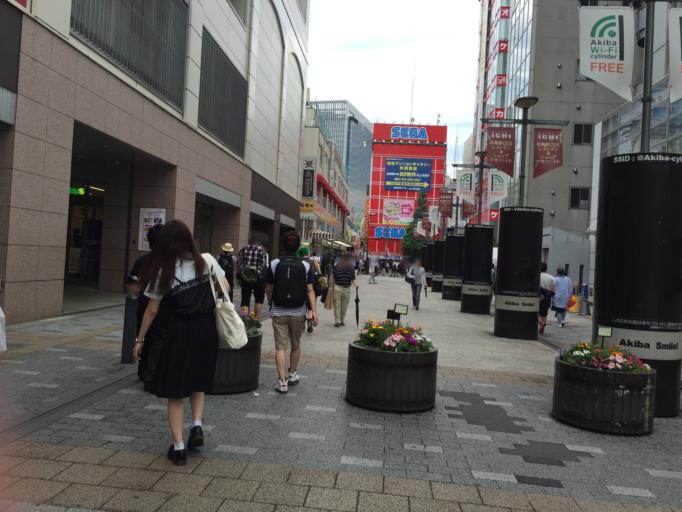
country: JP
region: Tokyo
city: Tokyo
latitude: 35.6986
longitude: 139.7724
